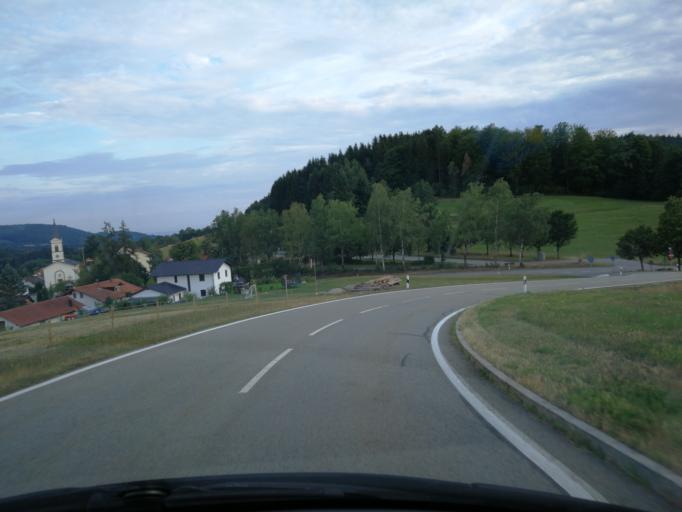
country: DE
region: Bavaria
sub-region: Lower Bavaria
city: Haibach
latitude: 49.0285
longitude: 12.7476
